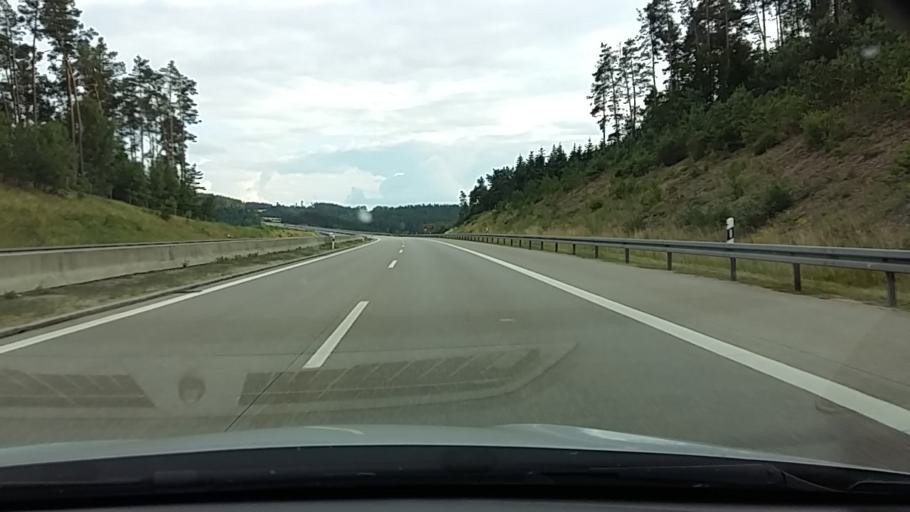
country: DE
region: Bavaria
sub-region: Upper Palatinate
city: Pfreimd
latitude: 49.4880
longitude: 12.1394
